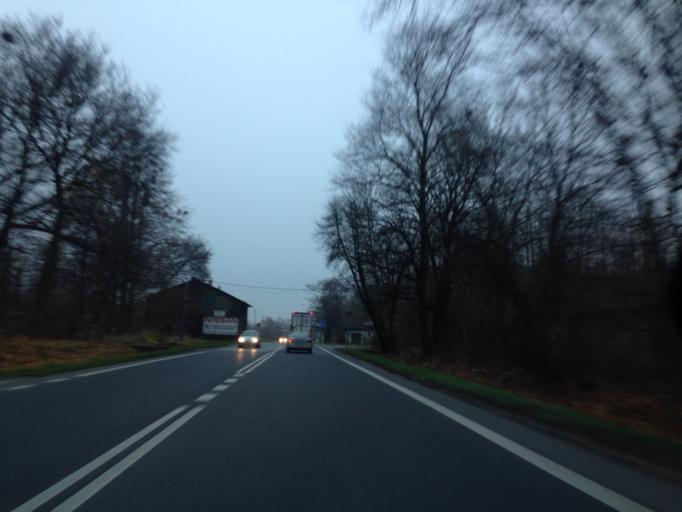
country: PL
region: Lodz Voivodeship
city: Lodz
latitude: 51.8053
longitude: 19.4969
